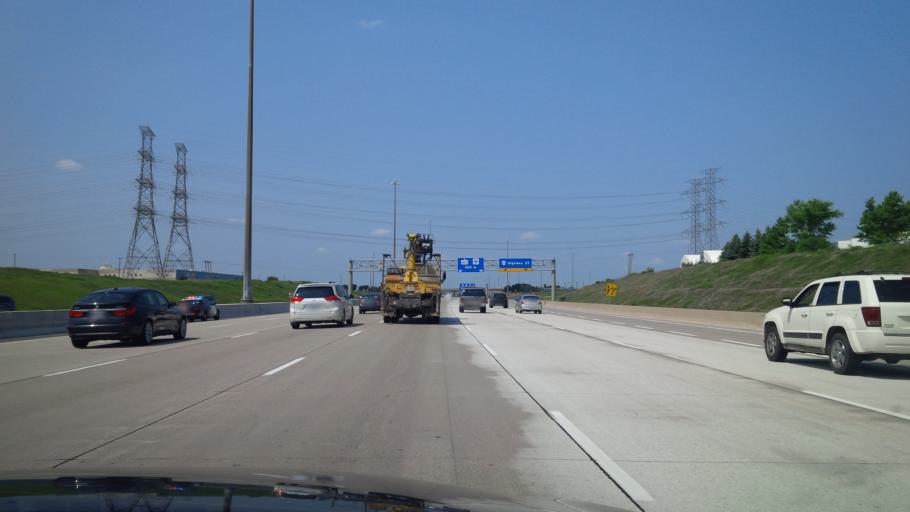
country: CA
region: Ontario
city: Etobicoke
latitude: 43.7608
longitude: -79.6065
